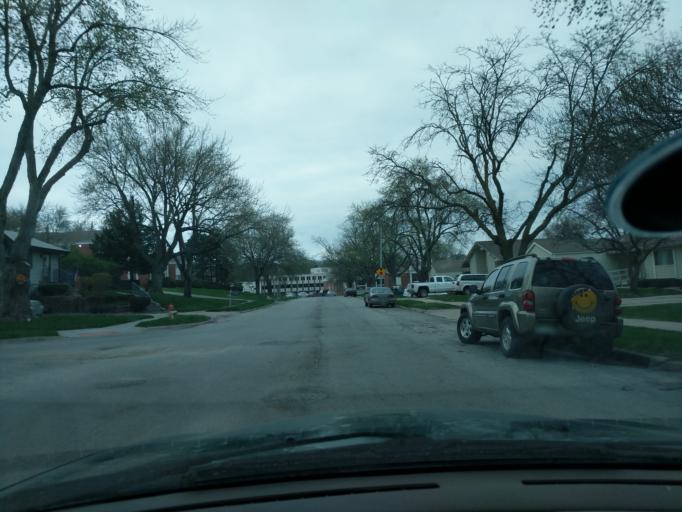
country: US
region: Nebraska
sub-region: Douglas County
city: Ralston
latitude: 41.2325
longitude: -96.0943
